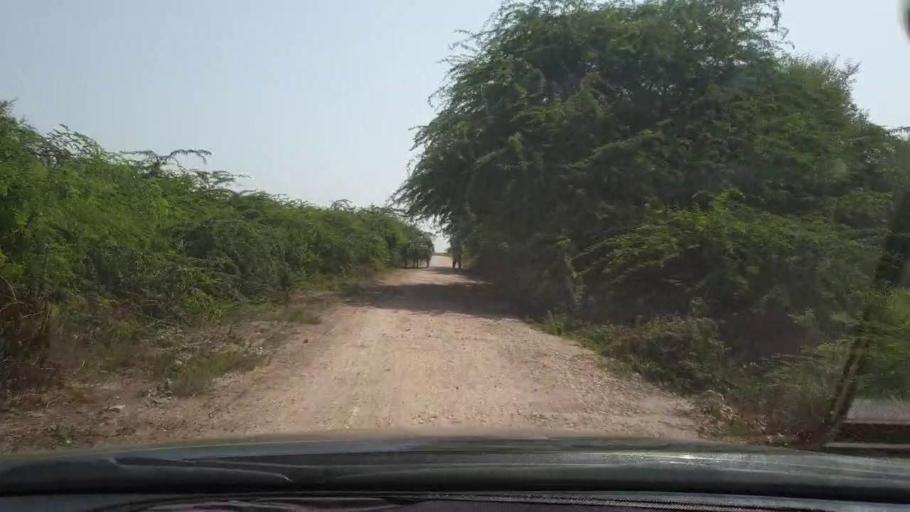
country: PK
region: Sindh
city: Naukot
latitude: 24.8117
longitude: 69.2442
